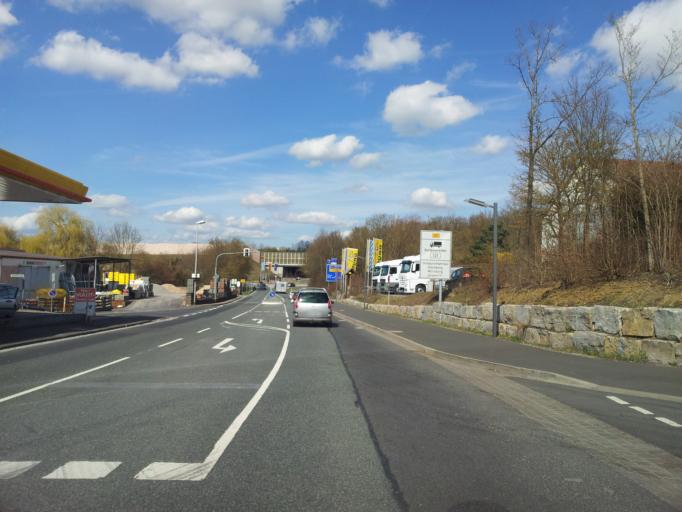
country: DE
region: Bavaria
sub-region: Regierungsbezirk Unterfranken
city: Kist
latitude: 49.7456
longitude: 9.8454
